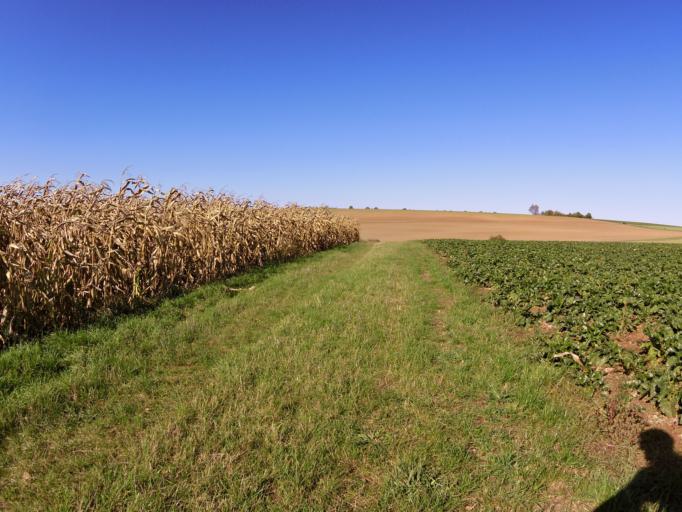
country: DE
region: Bavaria
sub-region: Regierungsbezirk Unterfranken
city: Theilheim
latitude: 49.7645
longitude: 10.0200
